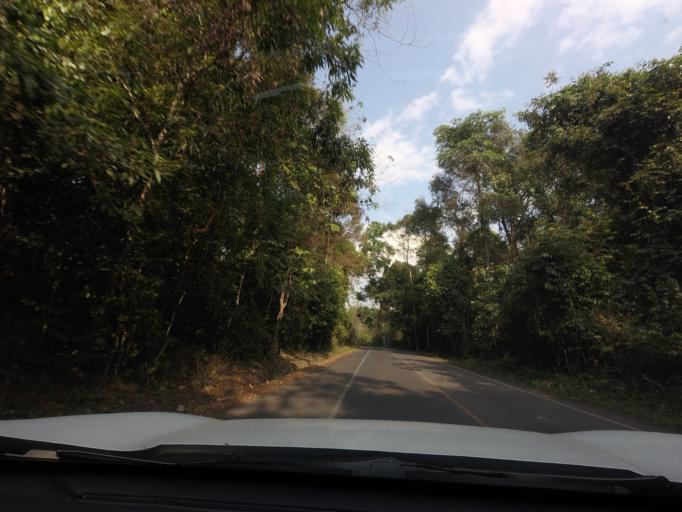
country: TH
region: Nakhon Nayok
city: Nakhon Nayok
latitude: 14.4197
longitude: 101.3838
